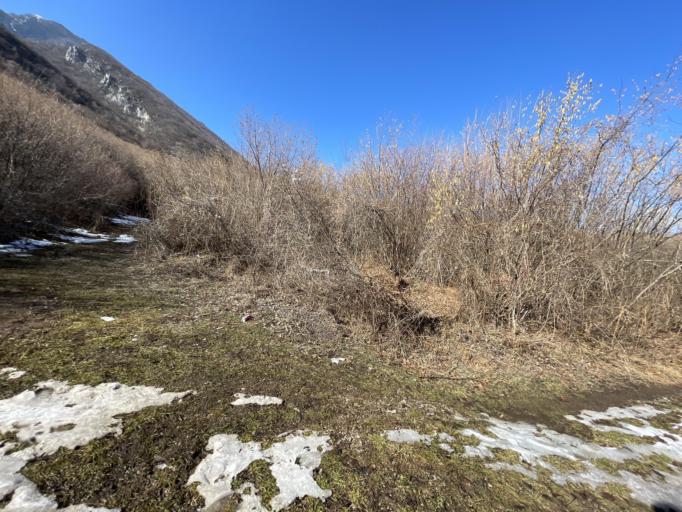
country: XK
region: Gjakova
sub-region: Komuna e Decanit
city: Strellc i Eperm
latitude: 42.6018
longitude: 20.2819
